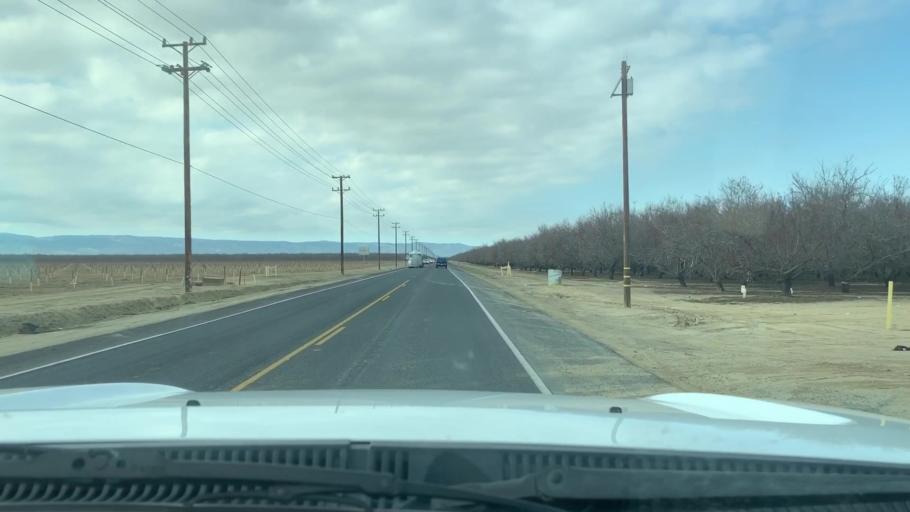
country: US
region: California
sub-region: Kern County
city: Lost Hills
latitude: 35.4992
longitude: -119.6901
